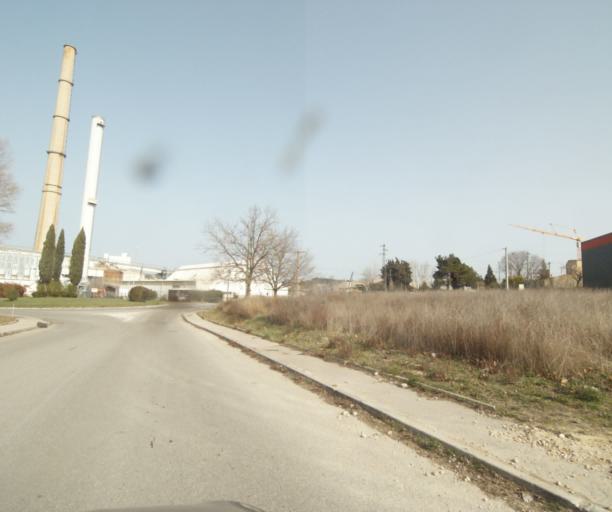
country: FR
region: Provence-Alpes-Cote d'Azur
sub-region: Departement des Bouches-du-Rhone
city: Gardanne
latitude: 43.4651
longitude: 5.4895
